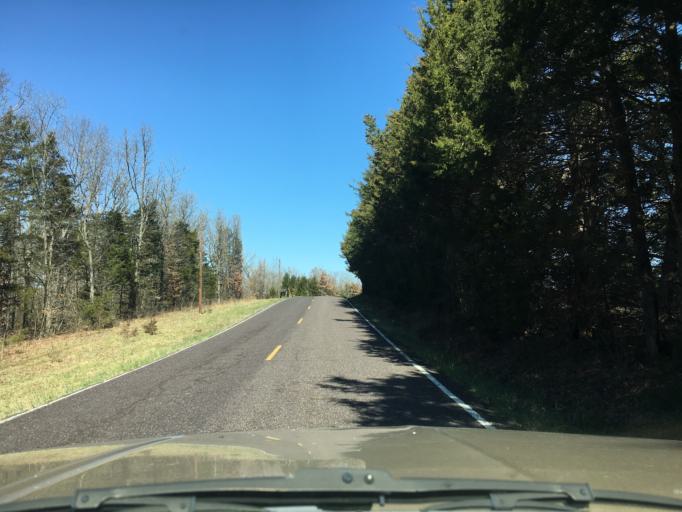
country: US
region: Missouri
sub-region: Franklin County
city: Gerald
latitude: 38.5201
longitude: -91.3281
